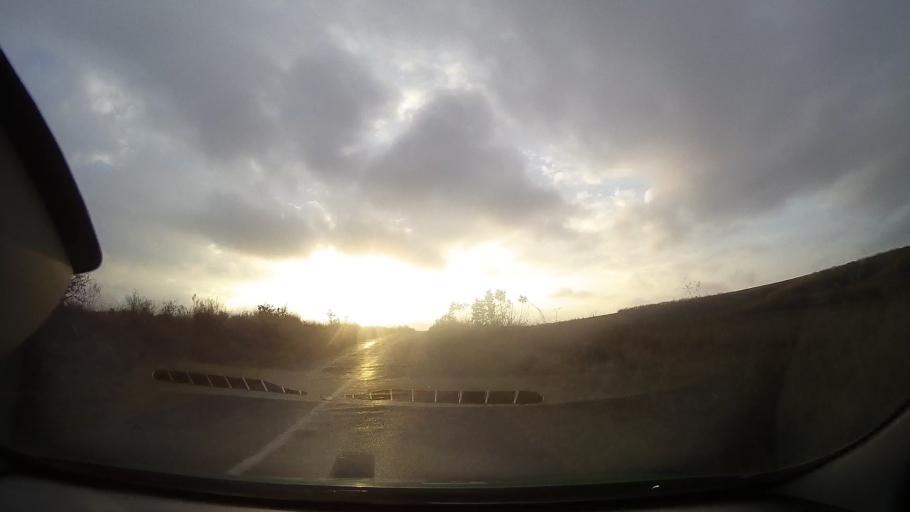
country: RO
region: Constanta
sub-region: Comuna Adamclisi
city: Adamclisi
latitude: 44.0336
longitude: 27.9309
